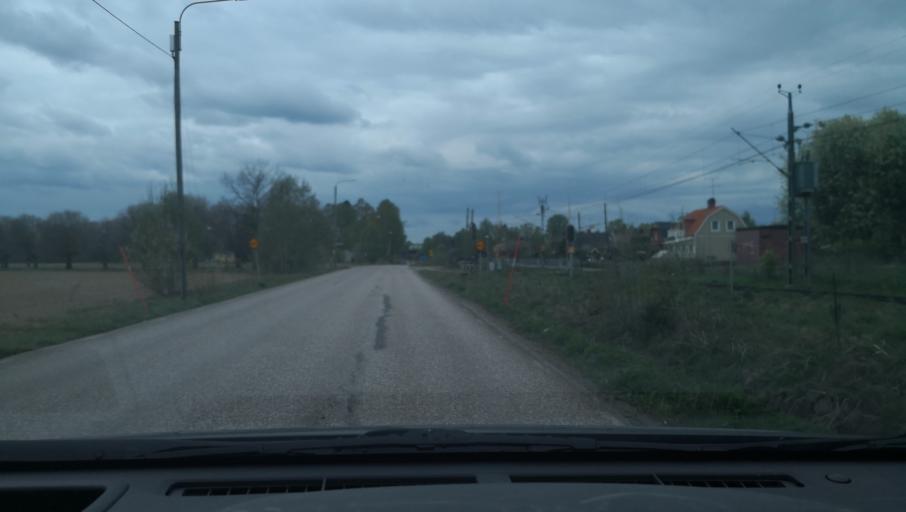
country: SE
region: Dalarna
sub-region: Avesta Kommun
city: Avesta
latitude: 60.1401
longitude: 16.2204
